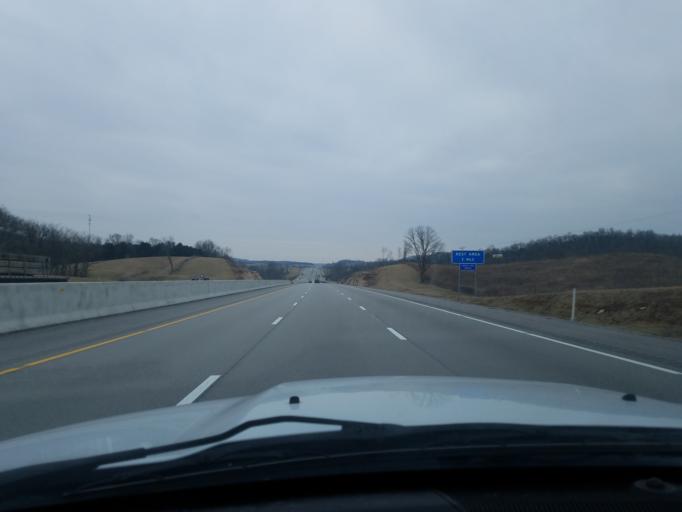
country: US
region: Kentucky
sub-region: Hart County
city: Munfordville
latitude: 37.2591
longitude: -85.9233
